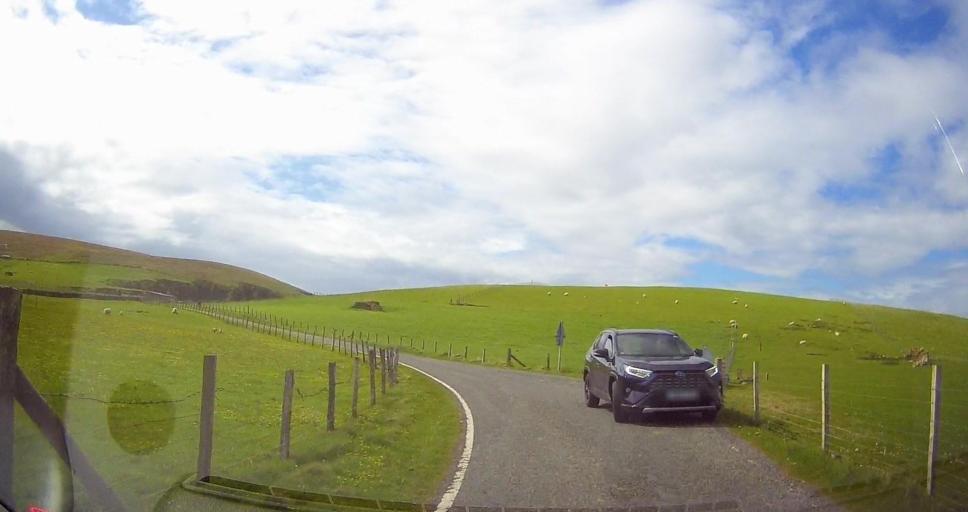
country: GB
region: Scotland
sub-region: Shetland Islands
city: Sandwick
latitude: 59.9432
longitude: -1.3407
